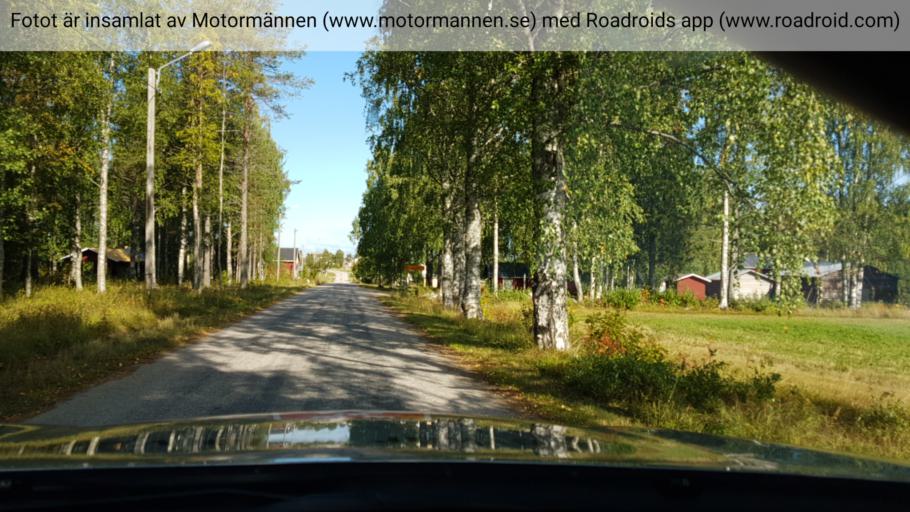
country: SE
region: Norrbotten
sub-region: Kalix Kommun
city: Kalix
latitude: 66.1773
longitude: 23.2144
